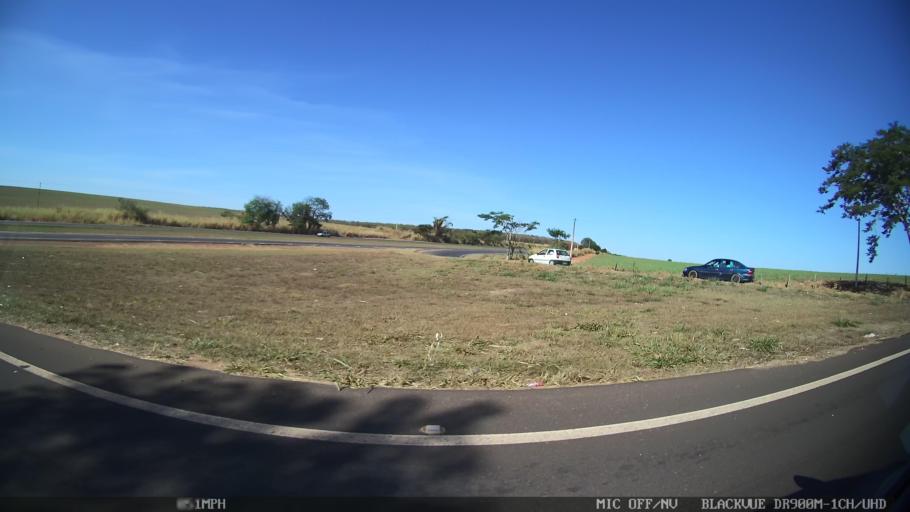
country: BR
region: Sao Paulo
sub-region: Olimpia
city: Olimpia
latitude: -20.7272
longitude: -48.8656
